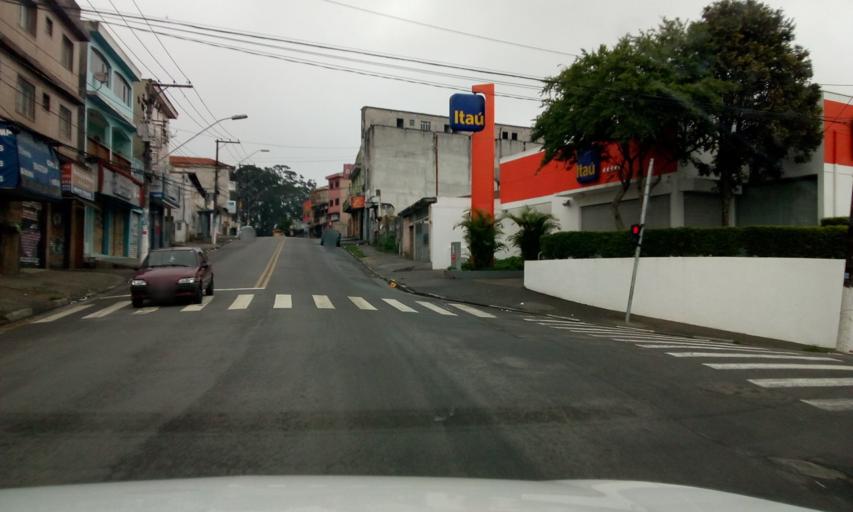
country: BR
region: Sao Paulo
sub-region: Diadema
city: Diadema
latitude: -23.6953
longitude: -46.6268
